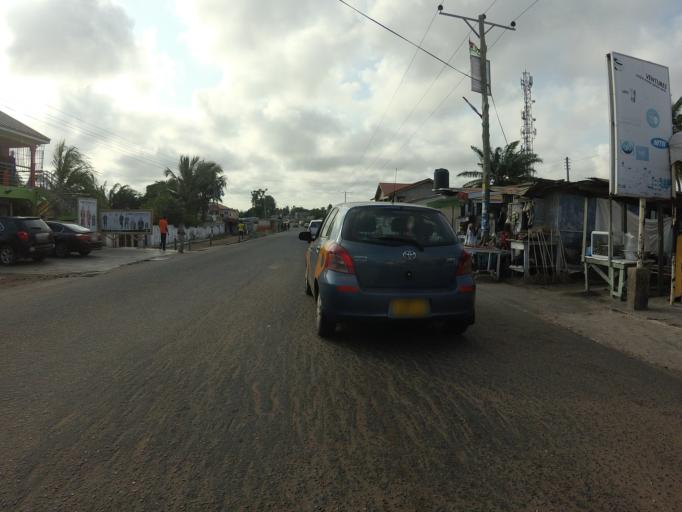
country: GH
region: Greater Accra
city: Nungua
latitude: 5.6162
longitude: -0.0767
